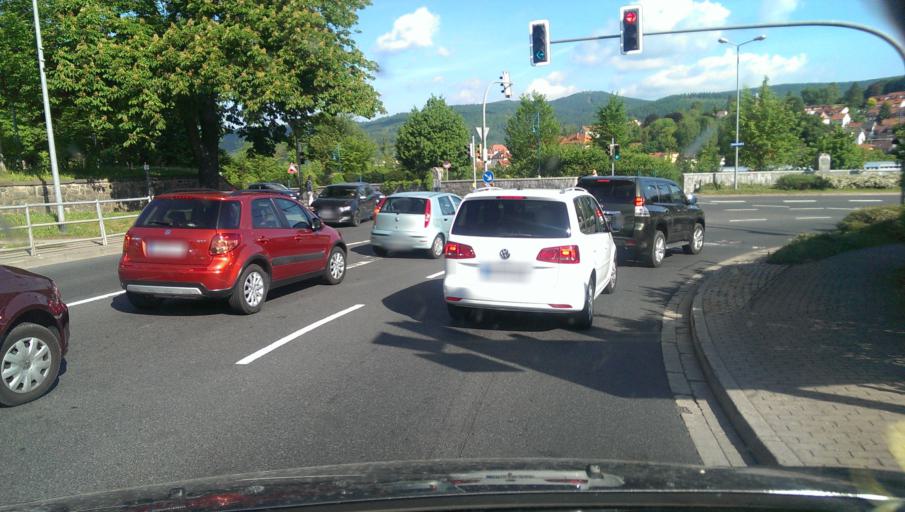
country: DE
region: Thuringia
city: Zella-Mehlis
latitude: 50.6520
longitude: 10.6689
